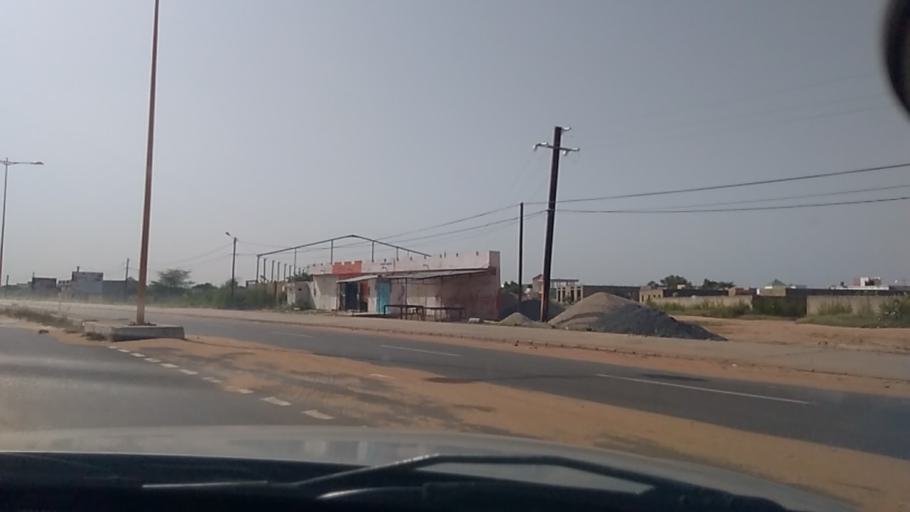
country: SN
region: Diourbel
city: Mbake
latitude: 14.8195
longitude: -15.9111
